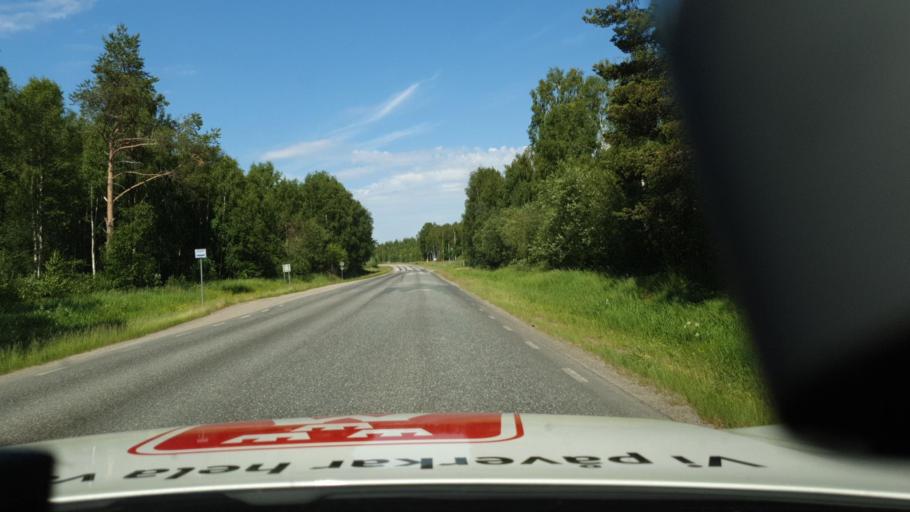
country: SE
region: Norrbotten
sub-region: Kalix Kommun
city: Rolfs
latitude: 65.8697
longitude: 23.1153
